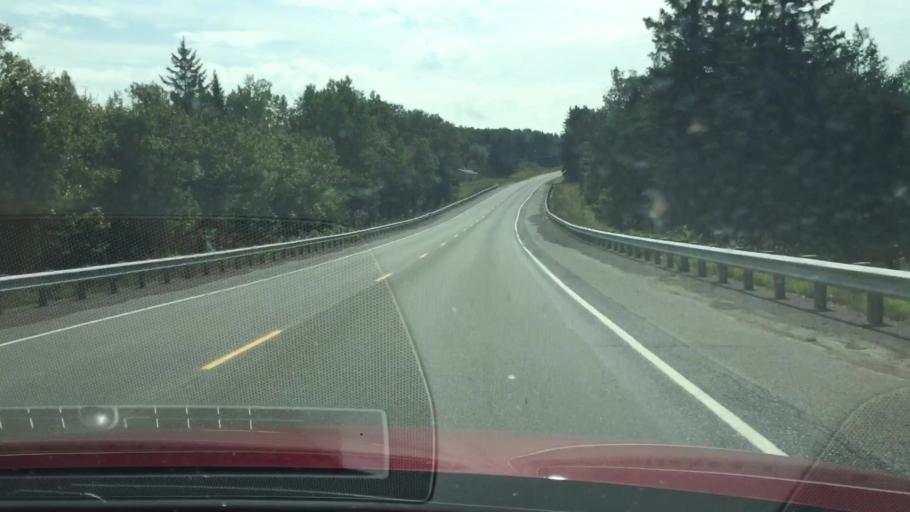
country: US
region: Maine
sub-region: Aroostook County
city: Easton
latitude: 46.5992
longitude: -67.9679
